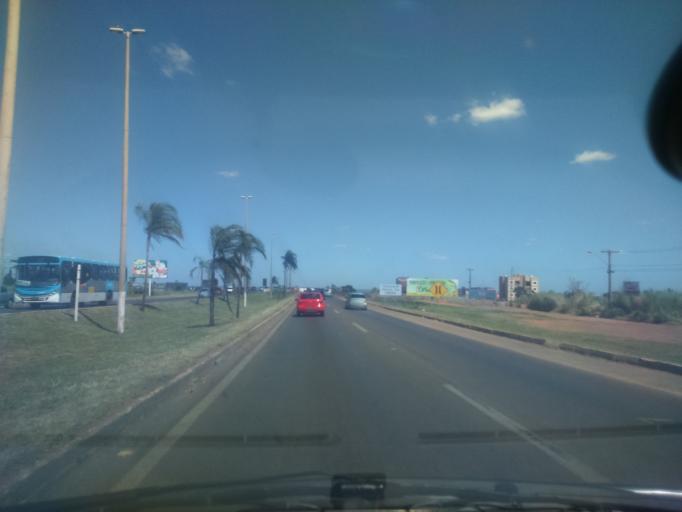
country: BR
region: Goias
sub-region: Luziania
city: Luziania
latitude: -16.0806
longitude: -47.9864
